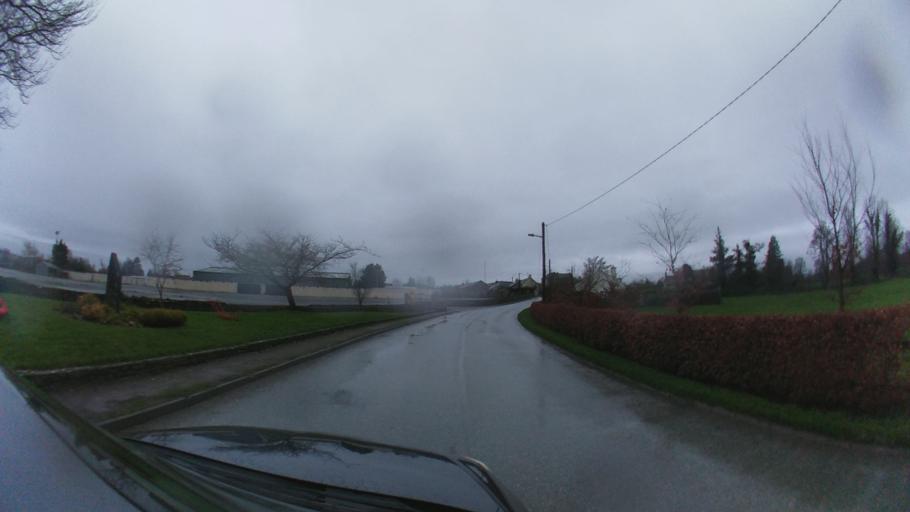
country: IE
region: Leinster
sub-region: County Carlow
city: Bagenalstown
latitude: 52.6322
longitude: -6.9934
